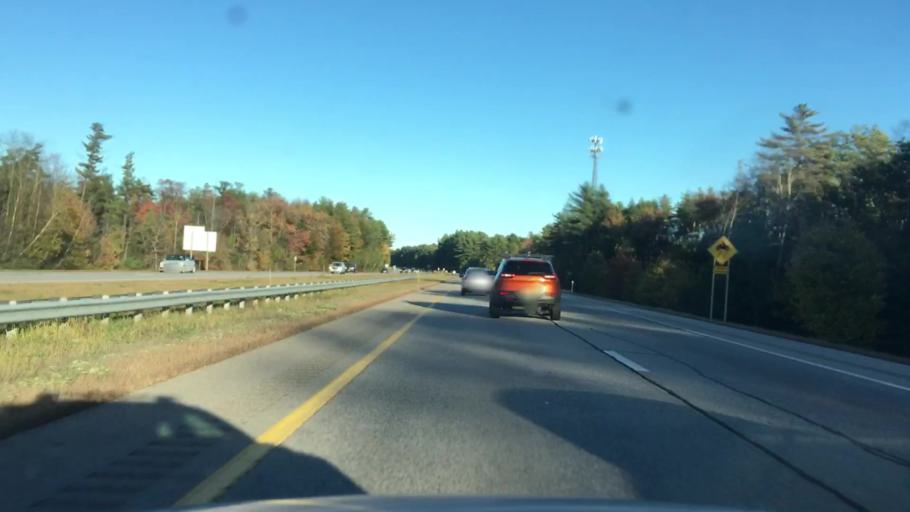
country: US
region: New Hampshire
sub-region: Rockingham County
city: Epping
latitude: 43.0254
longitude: -71.1023
